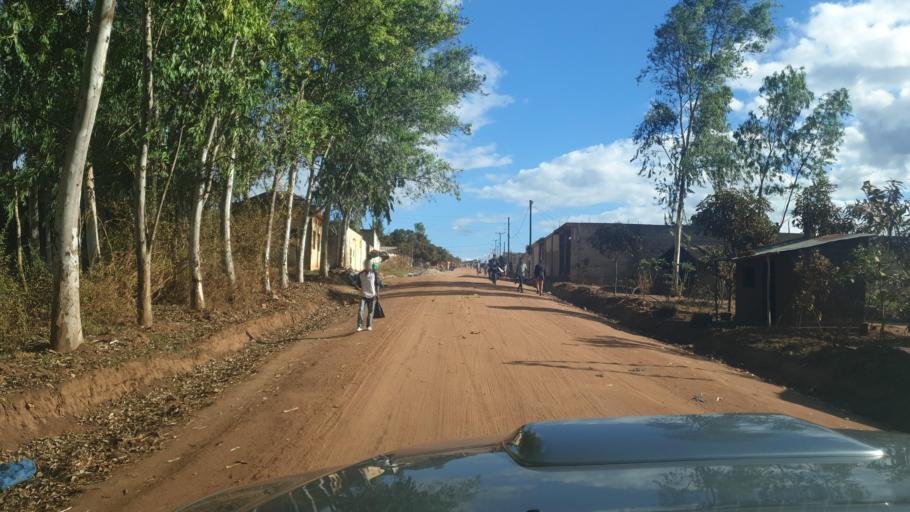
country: MZ
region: Nampula
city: Nampula
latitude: -15.0984
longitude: 39.2239
